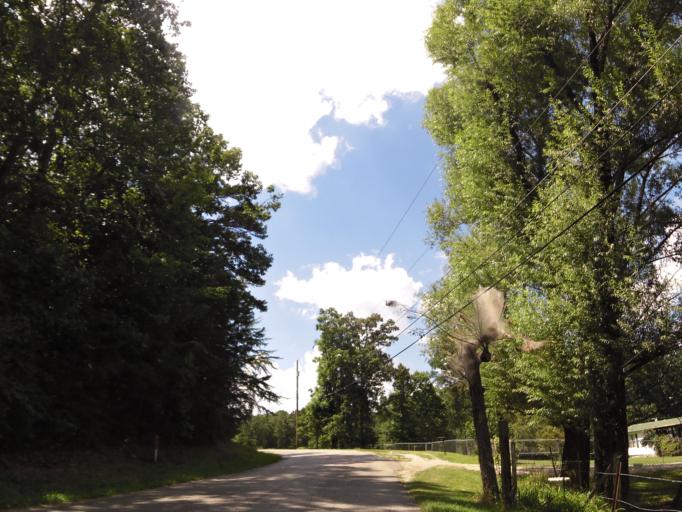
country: US
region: Tennessee
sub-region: Roane County
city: Rockwood
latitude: 35.8953
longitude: -84.7620
